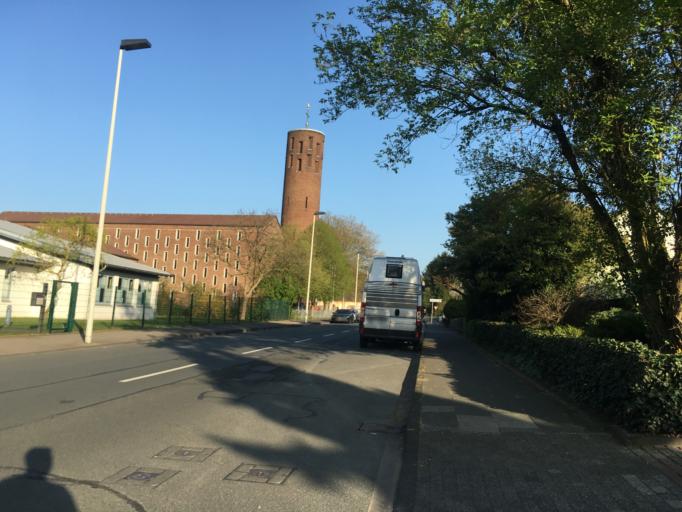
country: DE
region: North Rhine-Westphalia
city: Leichlingen
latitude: 51.1497
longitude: 7.0160
